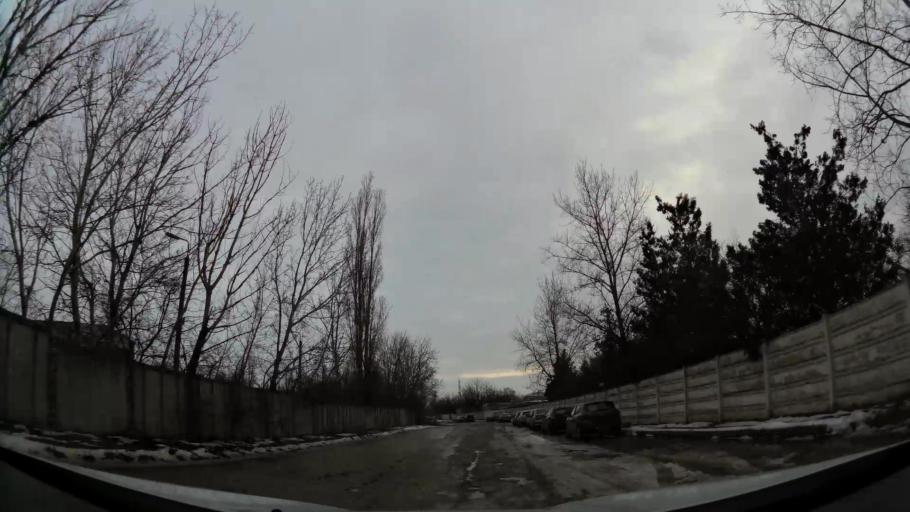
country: RO
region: Ilfov
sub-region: Comuna Glina
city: Catelu
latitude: 44.4014
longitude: 26.2019
